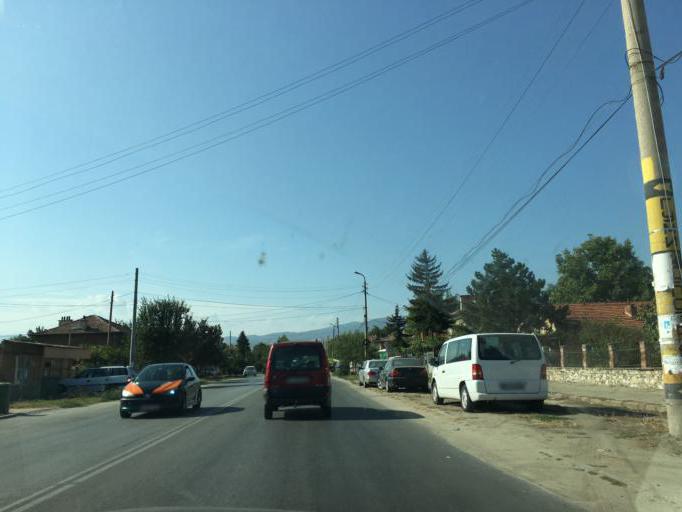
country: BG
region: Pazardzhik
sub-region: Obshtina Pazardzhik
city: Pazardzhik
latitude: 42.1594
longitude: 24.3136
